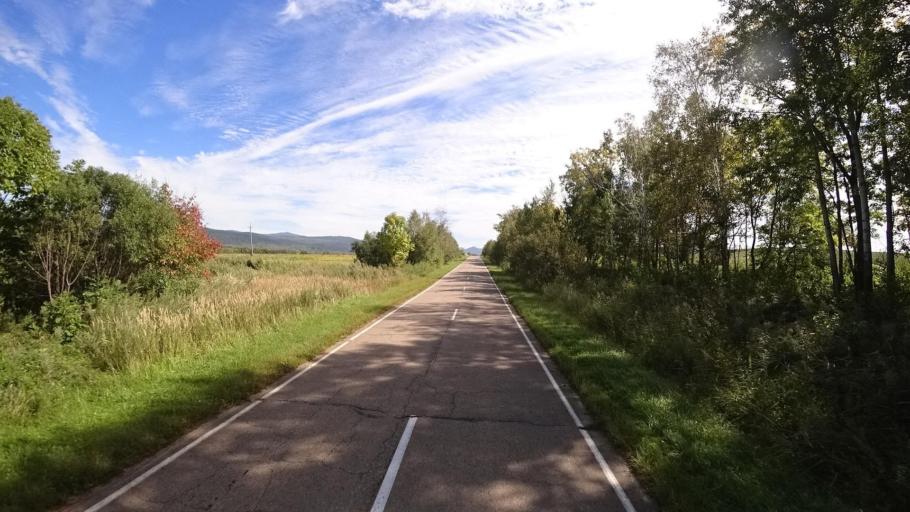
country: RU
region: Primorskiy
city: Yakovlevka
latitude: 44.4193
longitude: 133.5804
